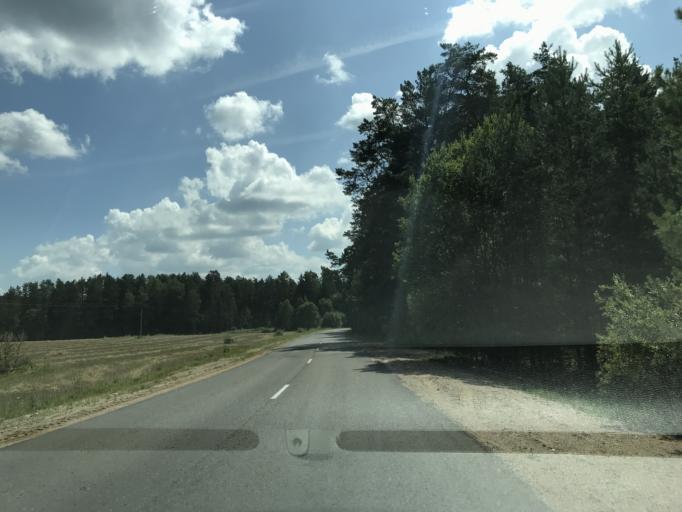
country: BY
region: Minsk
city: Rakaw
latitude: 54.0054
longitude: 26.9831
